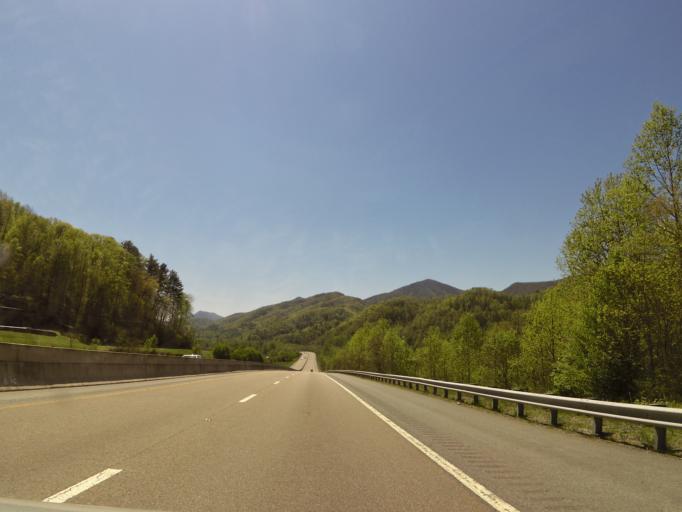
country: US
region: Tennessee
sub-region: Unicoi County
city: Banner Hill
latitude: 36.1067
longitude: -82.4605
